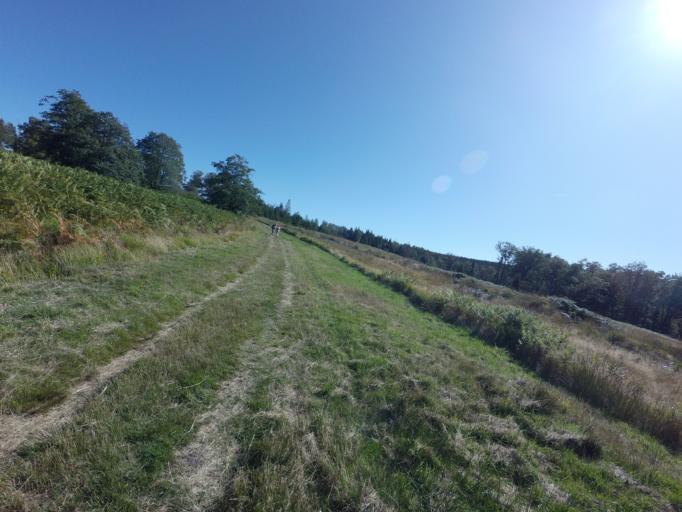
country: DE
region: North Rhine-Westphalia
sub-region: Regierungsbezirk Koln
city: Roetgen
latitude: 50.5927
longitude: 6.1474
